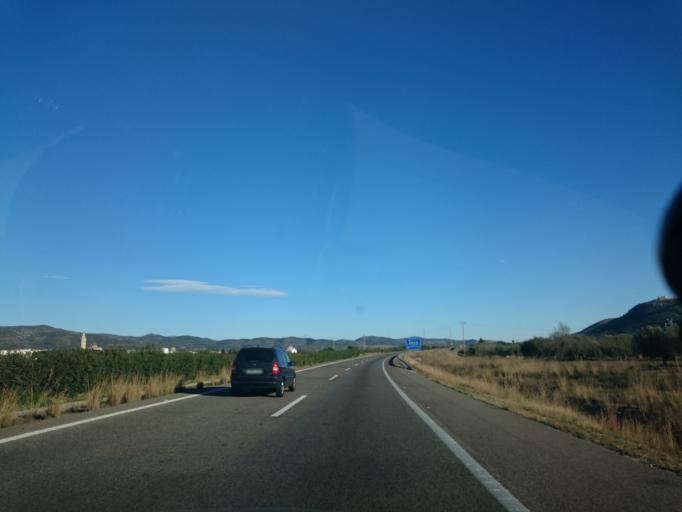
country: ES
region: Valencia
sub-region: Provincia de Castello
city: Alcala de Xivert
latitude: 40.2907
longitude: 0.2293
